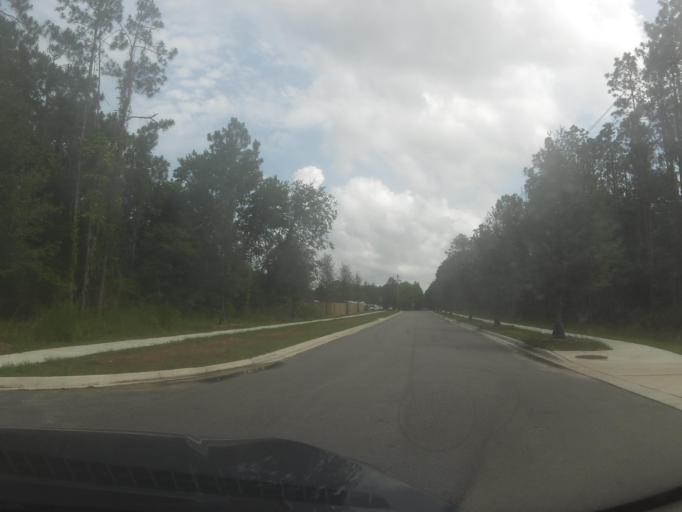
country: US
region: Florida
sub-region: Saint Johns County
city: Saint Augustine South
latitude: 29.8634
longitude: -81.3900
